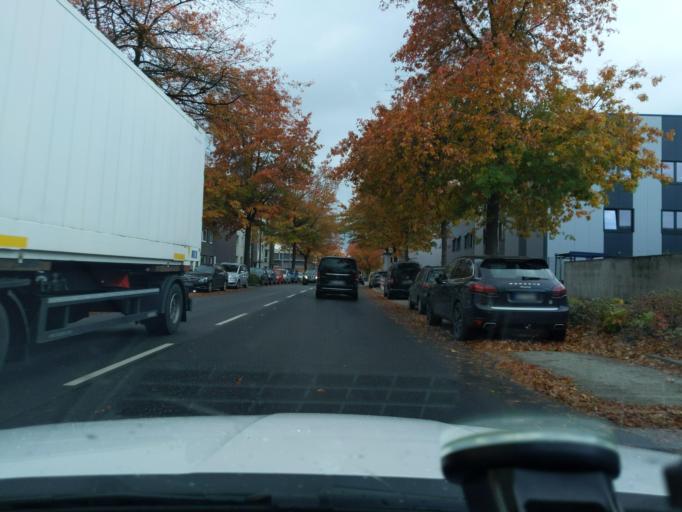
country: DE
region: North Rhine-Westphalia
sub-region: Regierungsbezirk Dusseldorf
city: Hilden
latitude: 51.1712
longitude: 6.8798
